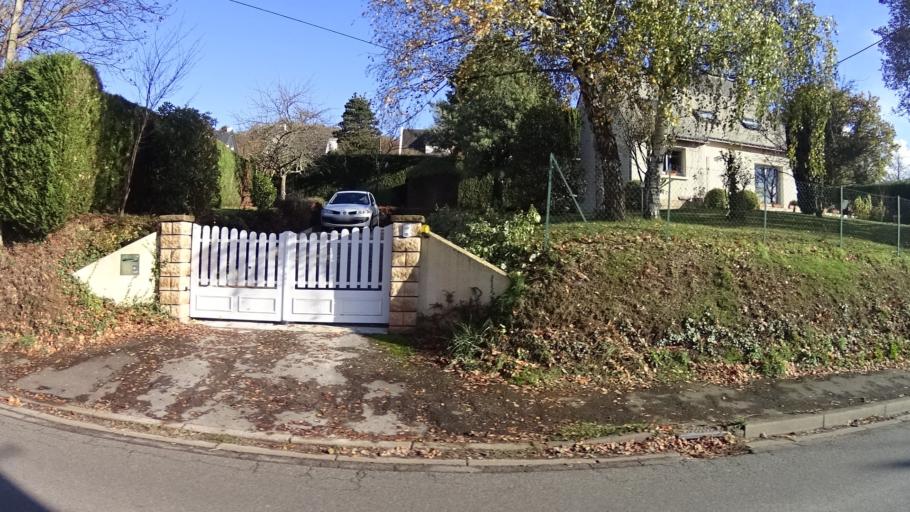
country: FR
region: Brittany
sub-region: Departement du Morbihan
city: Saint-Perreux
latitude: 47.6574
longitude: -2.0991
